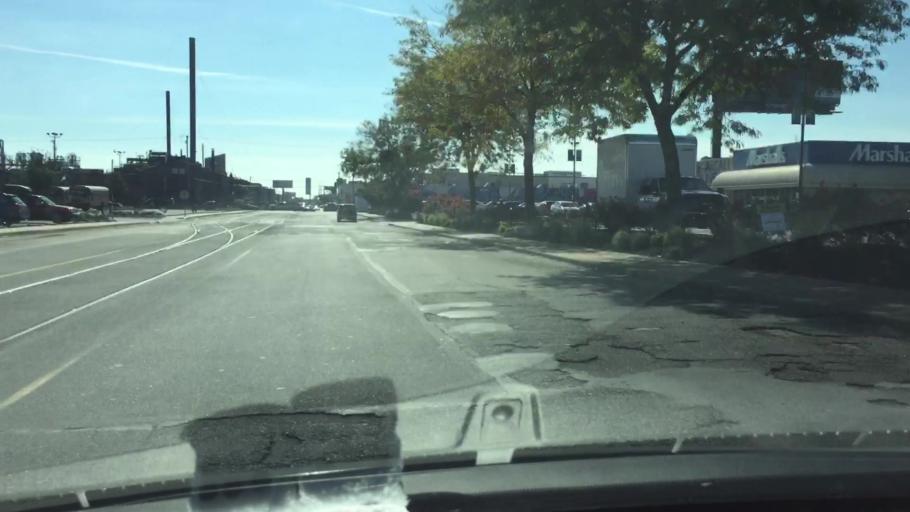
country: US
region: New Jersey
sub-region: Camden County
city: Camden
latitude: 39.9232
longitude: -75.1458
